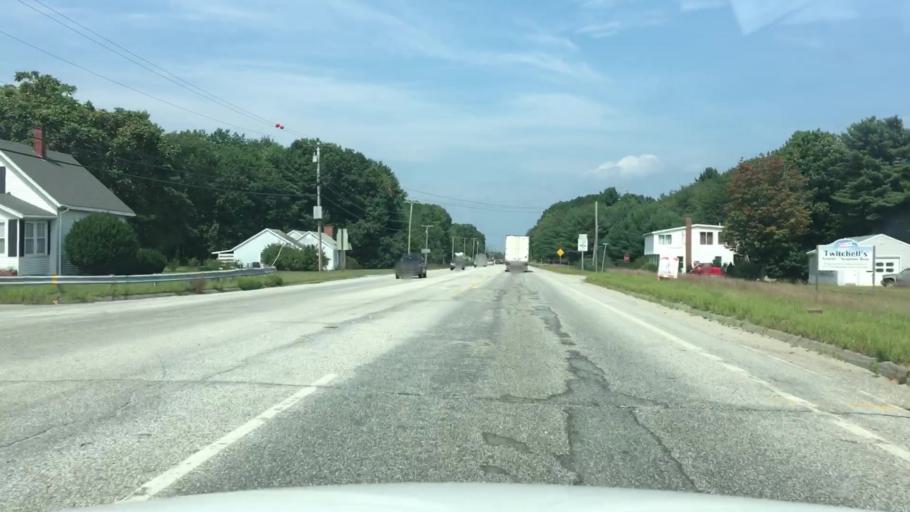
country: US
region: Maine
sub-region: Androscoggin County
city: Turner
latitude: 44.1894
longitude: -70.2380
